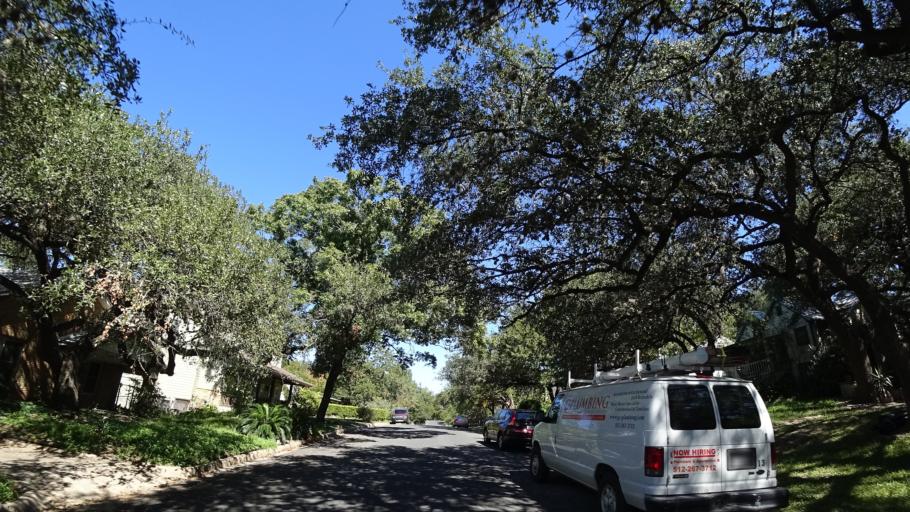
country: US
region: Texas
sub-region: Travis County
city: Austin
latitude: 30.2455
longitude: -97.7426
